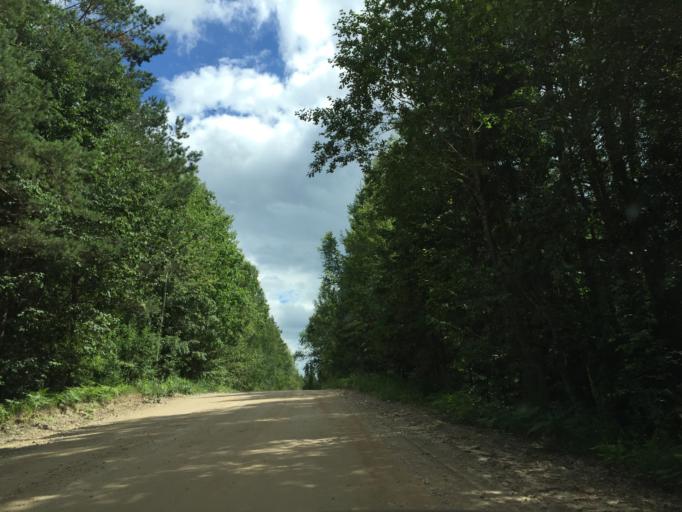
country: LV
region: Ropazu
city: Ropazi
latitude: 56.9136
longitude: 24.7530
